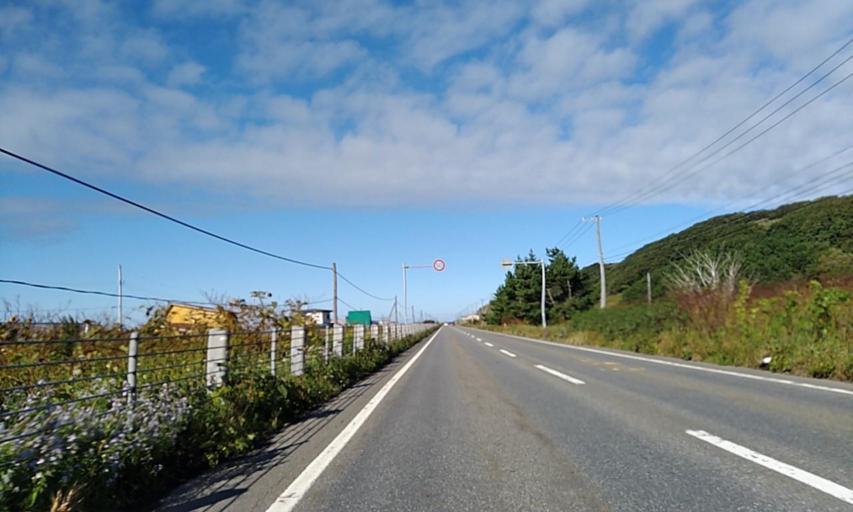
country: JP
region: Hokkaido
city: Shizunai-furukawacho
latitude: 42.3107
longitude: 142.4144
